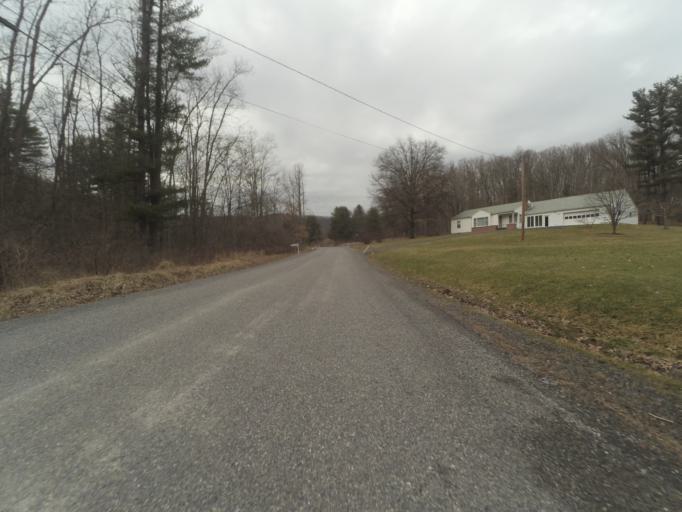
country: US
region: Pennsylvania
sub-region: Centre County
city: Stormstown
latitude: 40.8548
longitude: -77.9788
